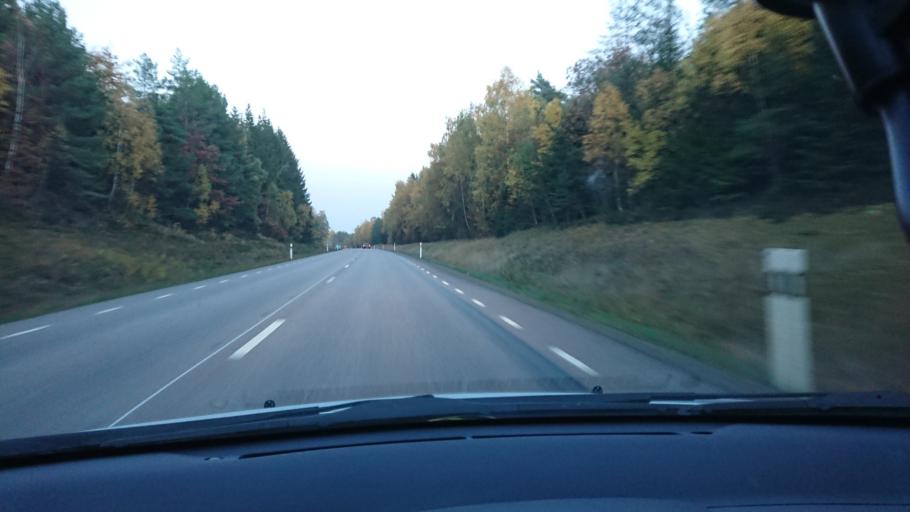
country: SE
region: Kronoberg
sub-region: Ljungby Kommun
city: Ljungby
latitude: 56.7566
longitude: 13.7543
